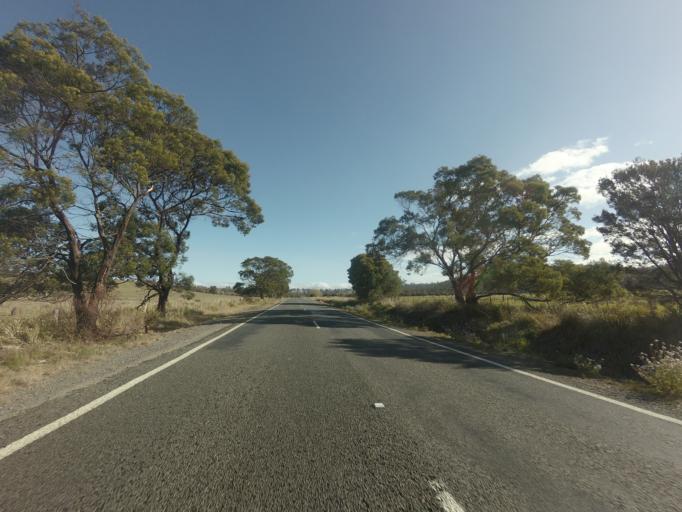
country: AU
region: Tasmania
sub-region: Sorell
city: Sorell
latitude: -42.4566
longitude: 147.9279
